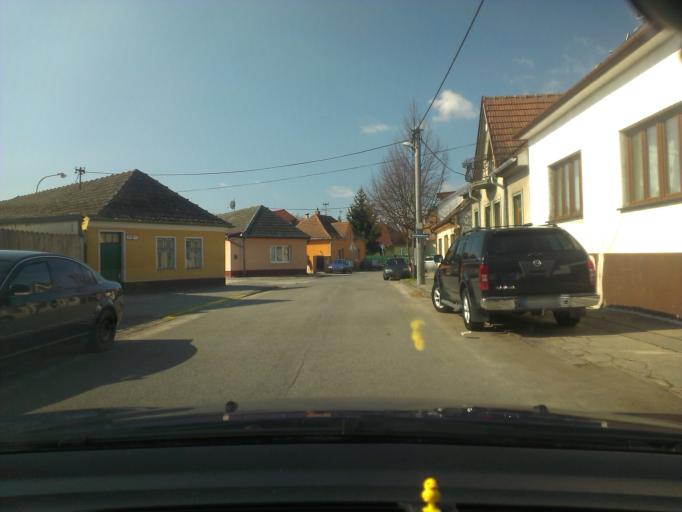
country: SK
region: Trnavsky
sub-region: Okres Trnava
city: Piestany
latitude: 48.5984
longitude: 17.8305
